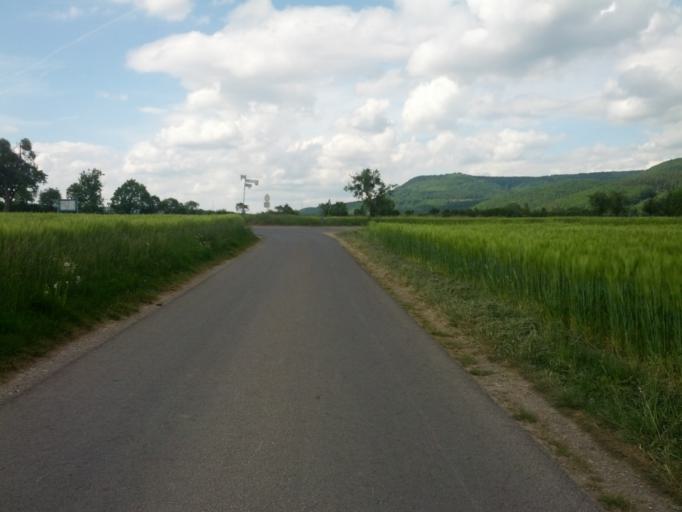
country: DE
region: Thuringia
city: Treffurt
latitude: 51.1323
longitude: 10.1972
